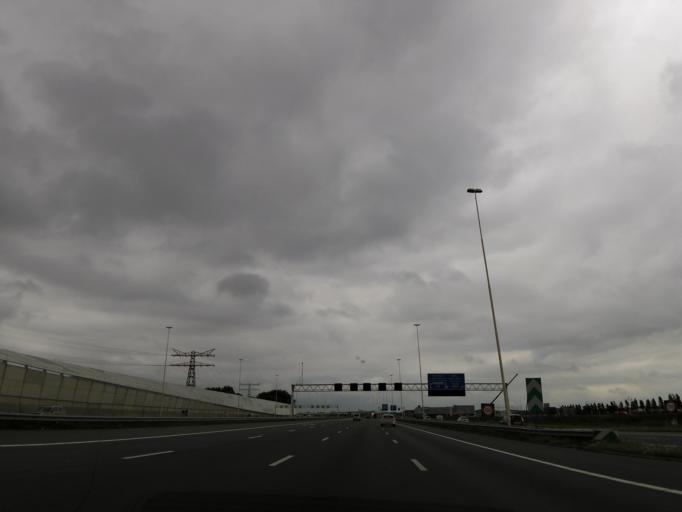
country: NL
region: Utrecht
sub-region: Stichtse Vecht
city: Spechtenkamp
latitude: 52.1230
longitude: 5.0232
